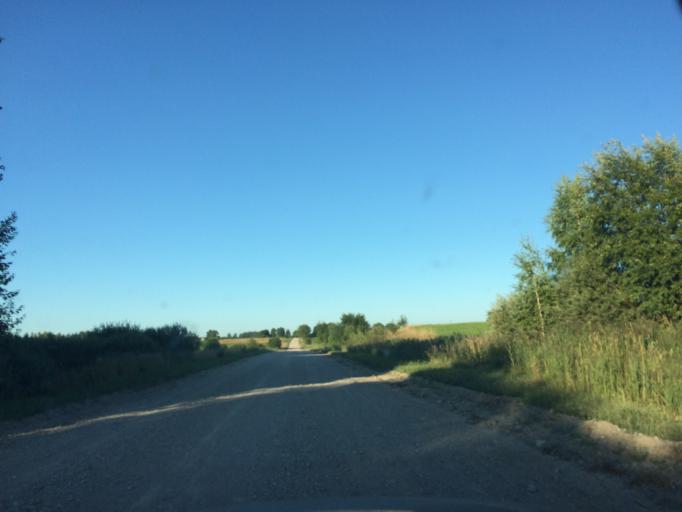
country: LV
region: Rezekne
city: Rezekne
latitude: 56.6205
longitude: 27.4816
